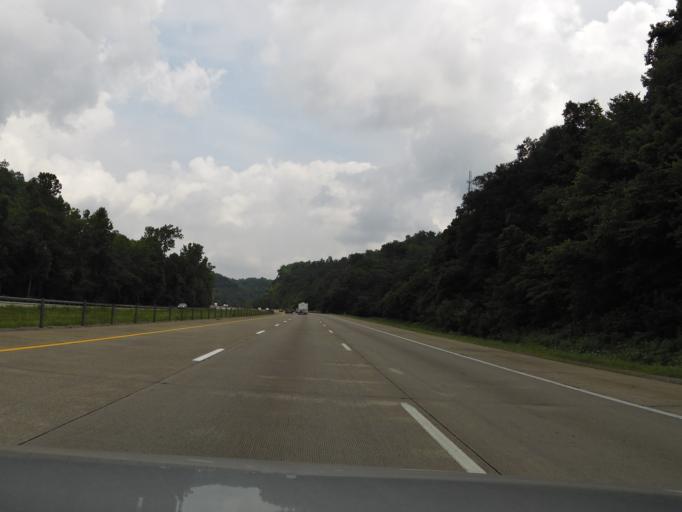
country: US
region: Kentucky
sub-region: Hardin County
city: Elizabethtown
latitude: 37.7609
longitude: -85.7952
